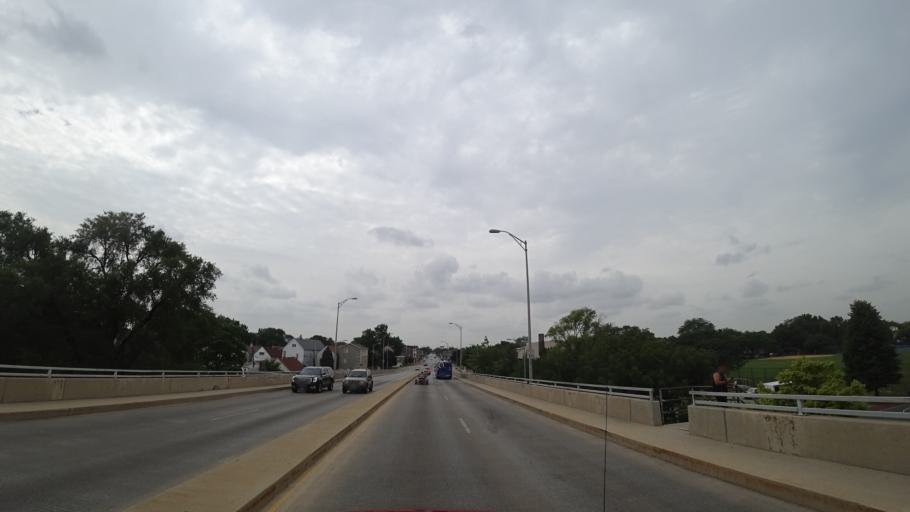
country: US
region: Illinois
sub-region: Cook County
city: Cicero
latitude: 41.8407
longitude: -87.7537
